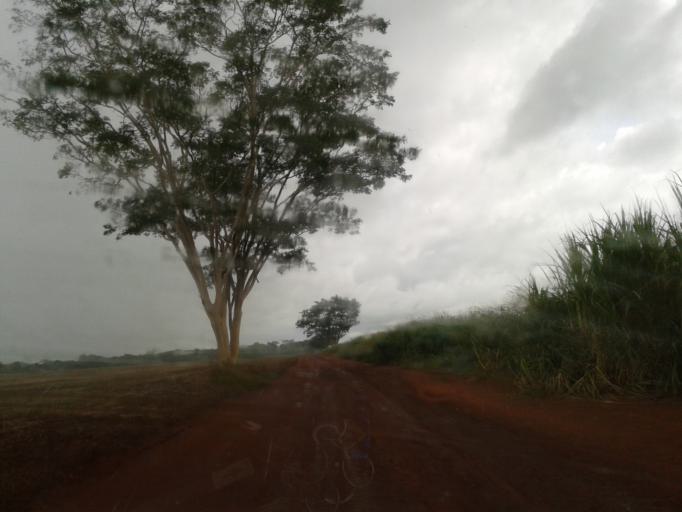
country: BR
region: Minas Gerais
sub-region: Santa Vitoria
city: Santa Vitoria
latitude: -18.6573
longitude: -49.9114
